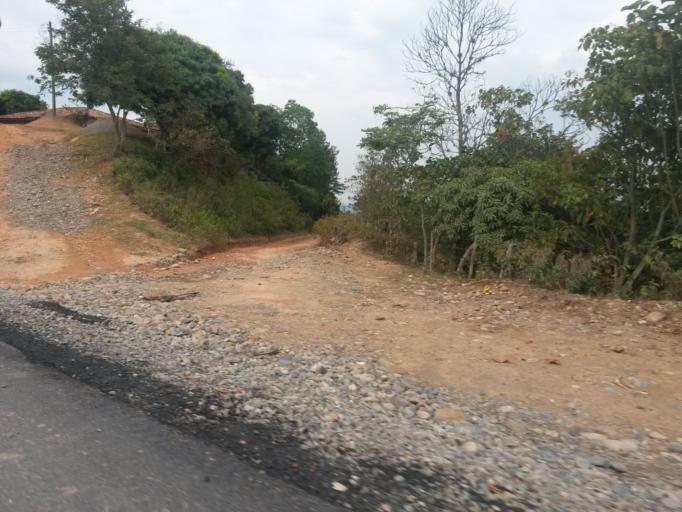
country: CO
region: Cauca
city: Buenos Aires
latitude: 3.0473
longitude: -76.6382
